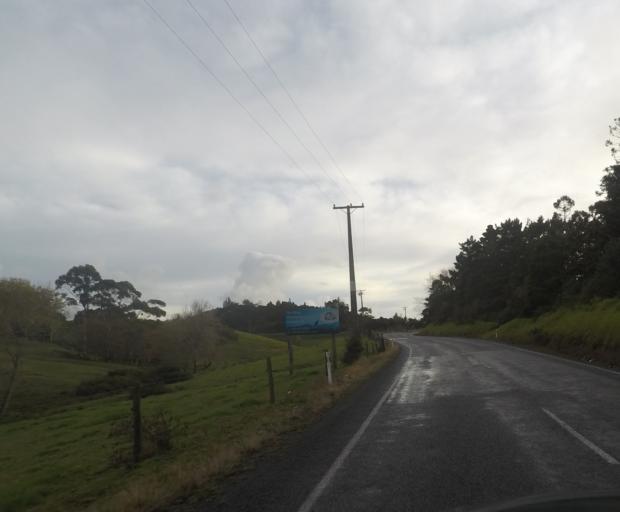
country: NZ
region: Auckland
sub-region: Auckland
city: Wellsford
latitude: -36.1699
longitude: 174.5804
